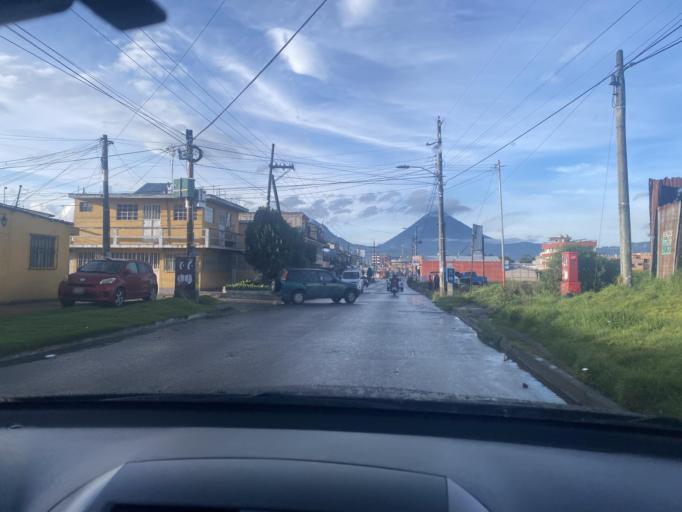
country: GT
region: Quetzaltenango
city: Olintepeque
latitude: 14.8644
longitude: -91.5215
